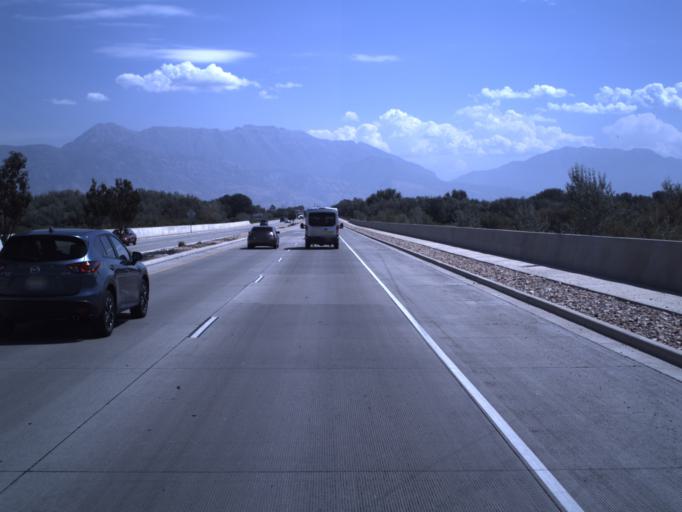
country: US
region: Utah
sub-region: Utah County
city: Saratoga Springs
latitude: 40.3762
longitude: -111.9002
